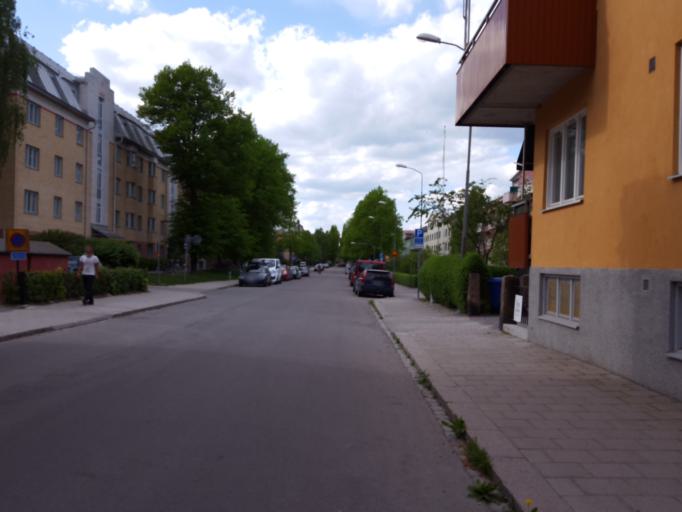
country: SE
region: Uppsala
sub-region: Uppsala Kommun
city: Uppsala
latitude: 59.8633
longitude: 17.6486
